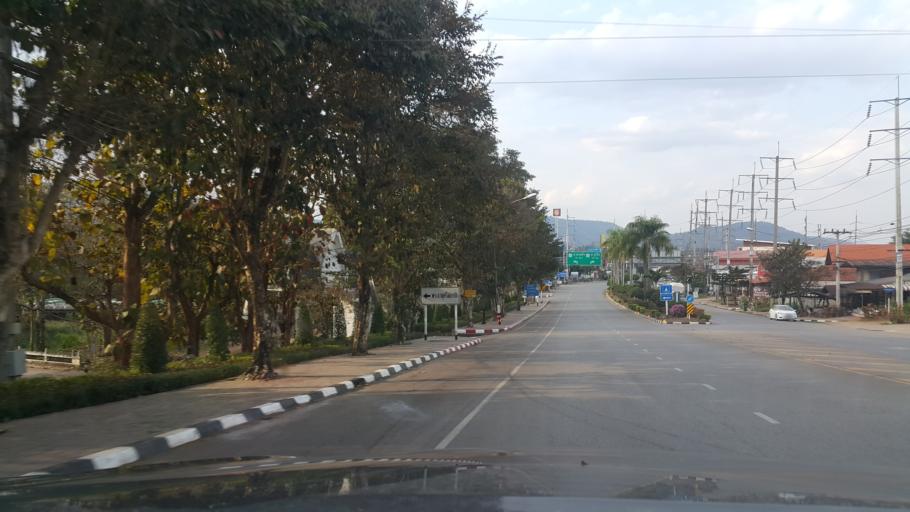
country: TH
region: Loei
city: Dan Sai
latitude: 17.2700
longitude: 101.1439
